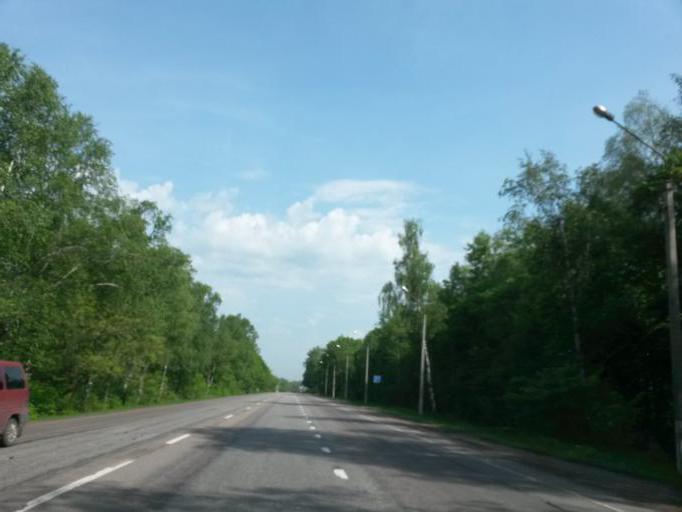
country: RU
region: Moskovskaya
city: Stolbovaya
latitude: 55.2107
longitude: 37.5066
